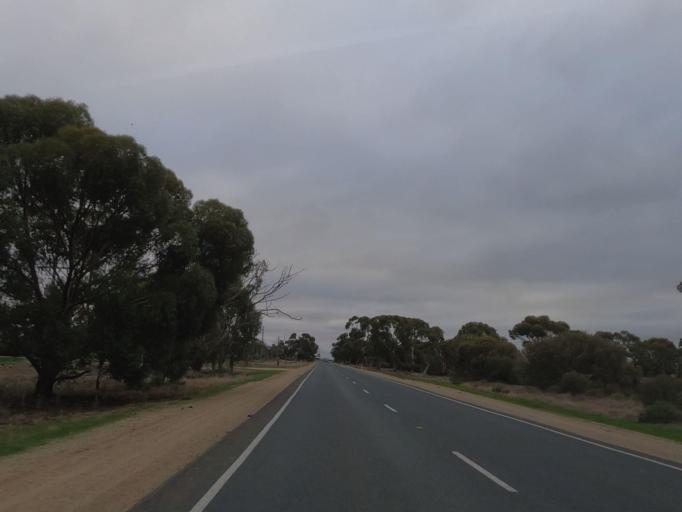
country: AU
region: Victoria
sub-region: Swan Hill
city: Swan Hill
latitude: -35.3999
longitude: 143.5764
